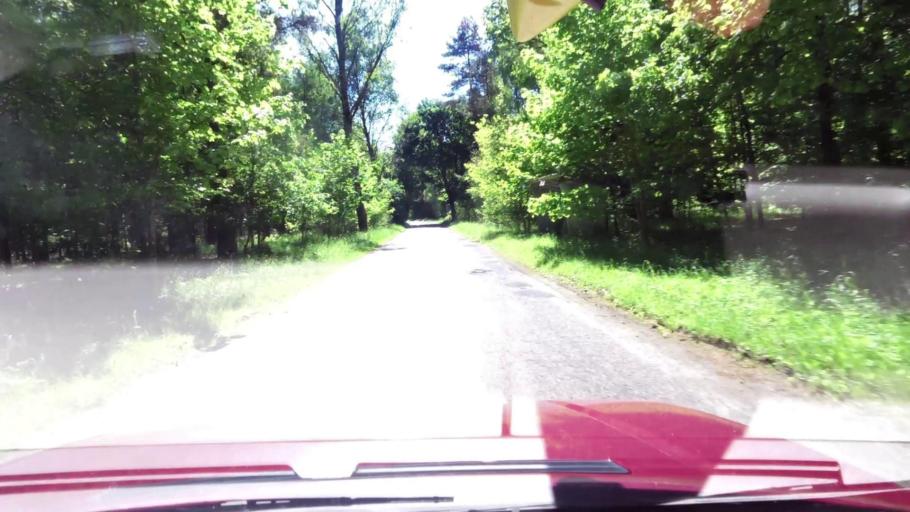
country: PL
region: West Pomeranian Voivodeship
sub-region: Powiat koszalinski
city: Bobolice
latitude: 54.0450
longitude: 16.5924
